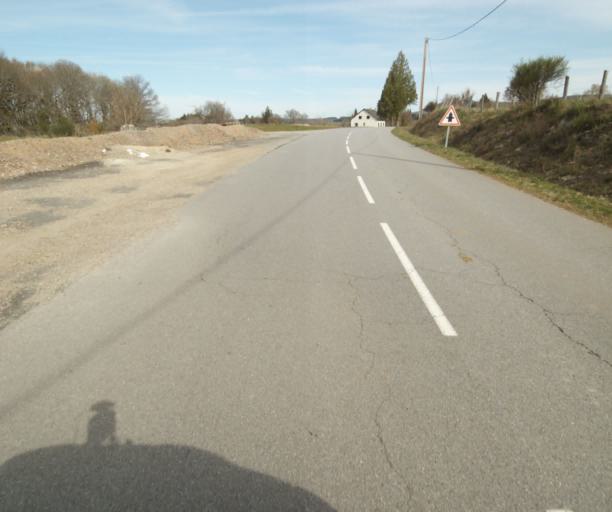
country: FR
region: Limousin
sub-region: Departement de la Correze
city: Correze
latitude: 45.4009
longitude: 1.8256
